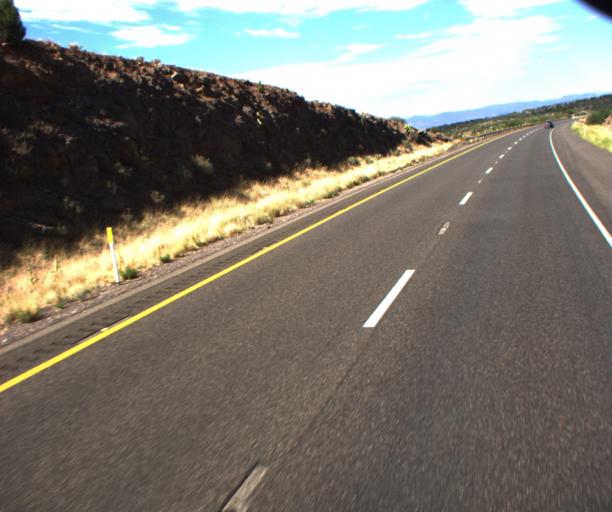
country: US
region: Arizona
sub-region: Yavapai County
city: Big Park
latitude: 34.7246
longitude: -111.7141
